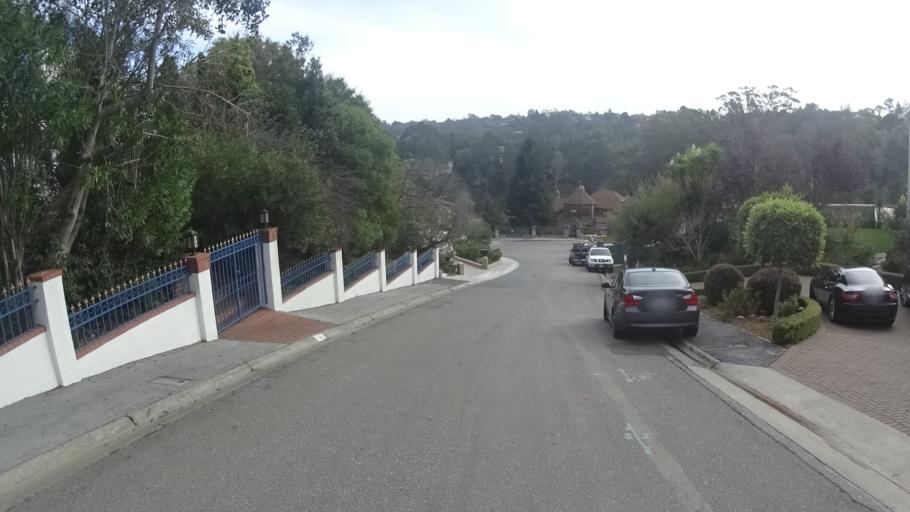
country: US
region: California
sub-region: San Mateo County
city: Hillsborough
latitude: 37.5658
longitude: -122.3791
